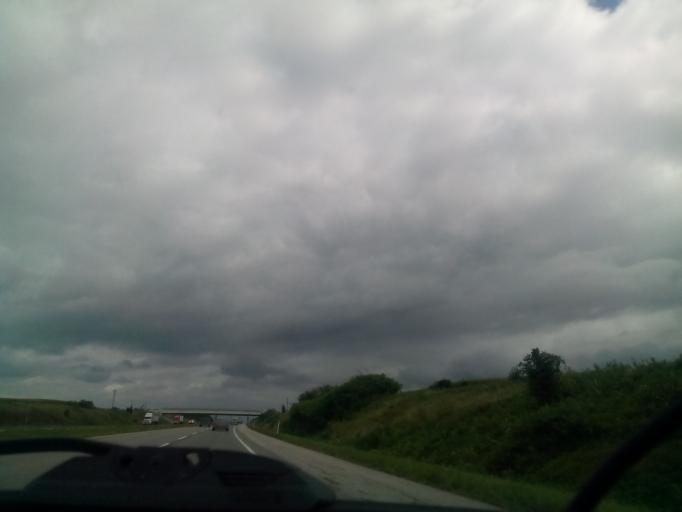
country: US
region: Indiana
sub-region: Steuben County
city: Fremont
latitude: 41.6834
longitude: -84.8817
